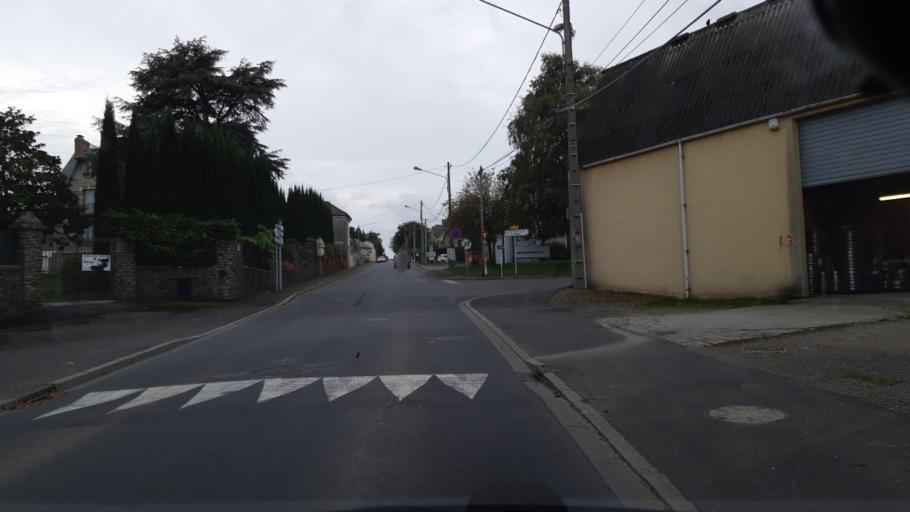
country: FR
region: Lower Normandy
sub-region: Departement de la Manche
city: Quettreville-sur-Sienne
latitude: 48.9205
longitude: -1.4282
